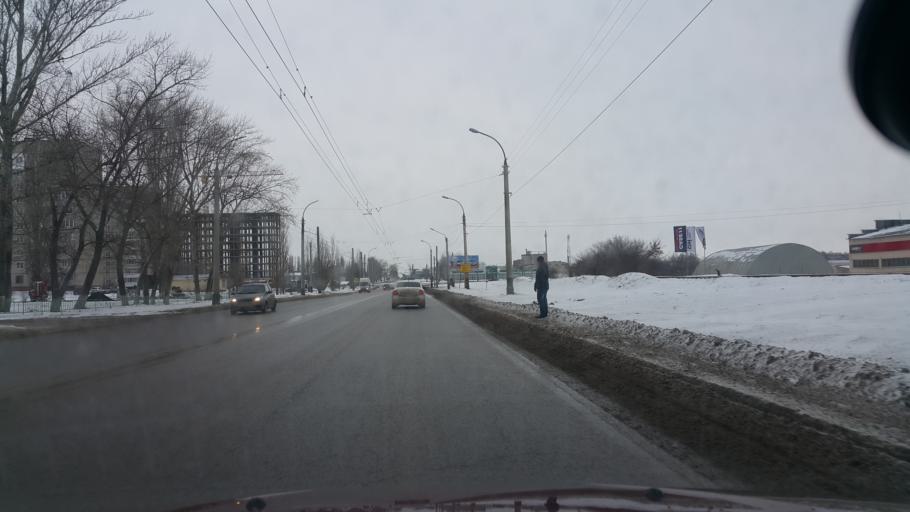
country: RU
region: Tambov
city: Tambov
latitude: 52.7376
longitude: 41.3816
